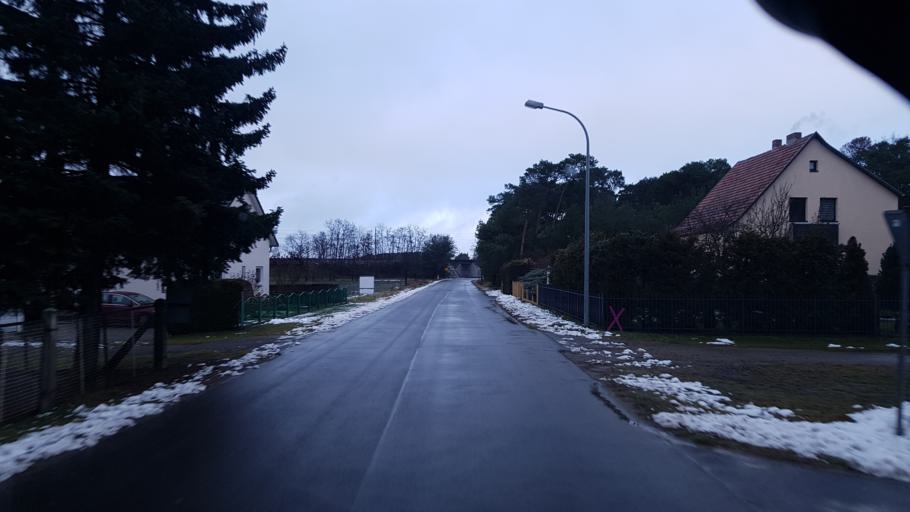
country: DE
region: Brandenburg
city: Janschwalde
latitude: 51.8666
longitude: 14.5091
